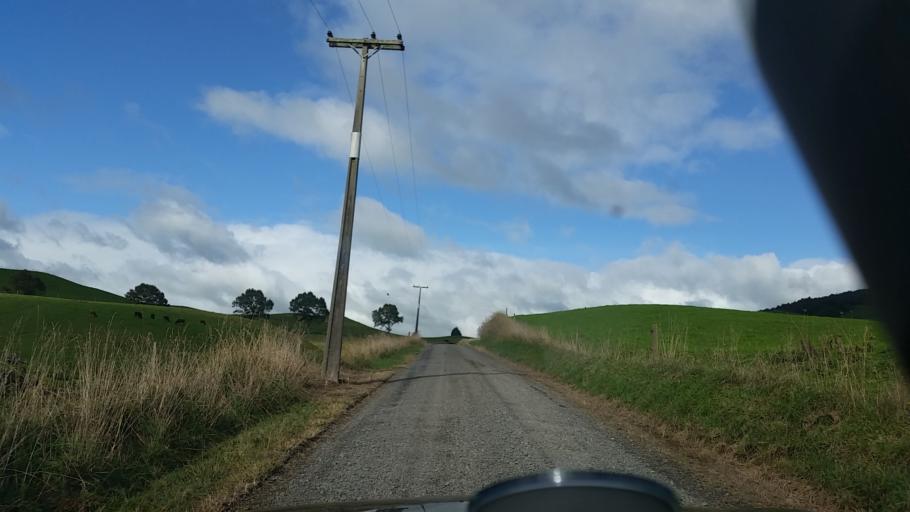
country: NZ
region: Waikato
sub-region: Matamata-Piako District
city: Matamata
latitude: -37.8168
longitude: 175.6738
